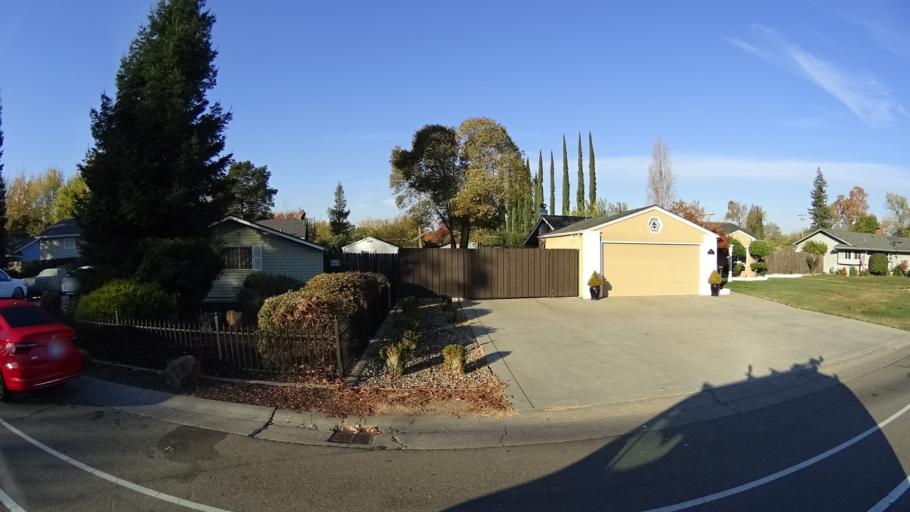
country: US
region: California
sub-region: Sacramento County
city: Antelope
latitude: 38.7045
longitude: -121.3088
